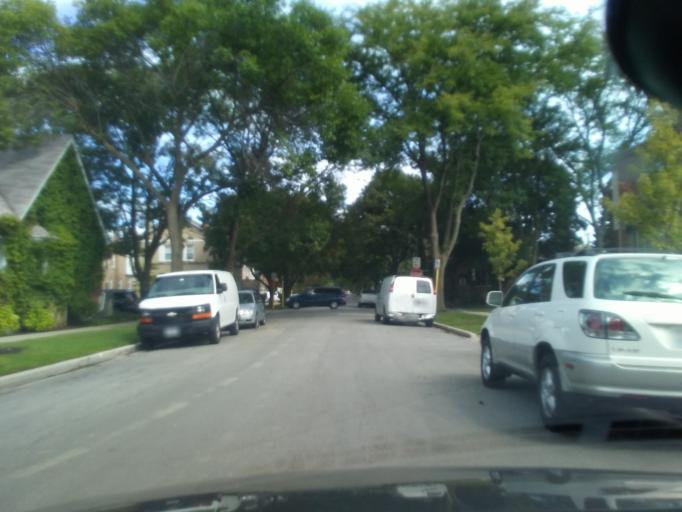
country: US
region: Illinois
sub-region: Cook County
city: Lincolnwood
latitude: 42.0090
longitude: -87.7021
